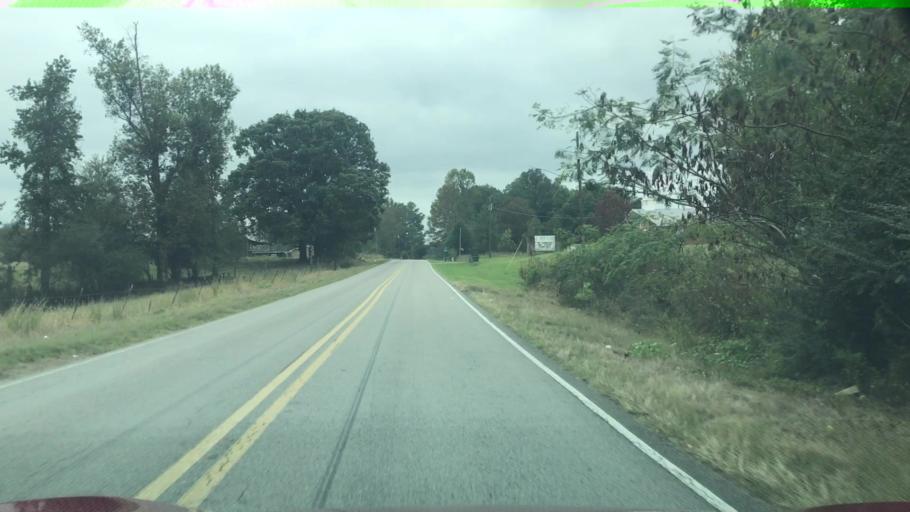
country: US
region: Alabama
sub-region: Cullman County
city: Good Hope
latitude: 34.1017
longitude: -87.0388
